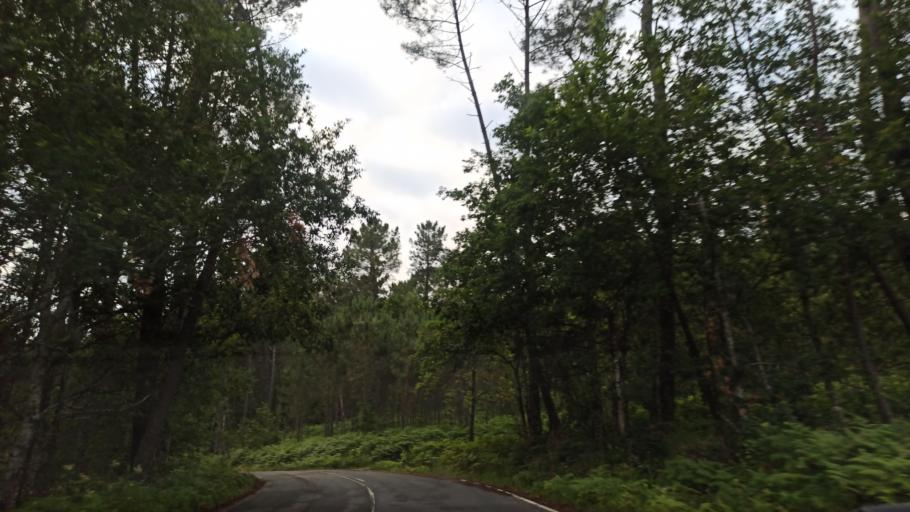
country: ES
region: Galicia
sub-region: Provincia da Coruna
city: Santiso
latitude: 42.8223
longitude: -8.1248
